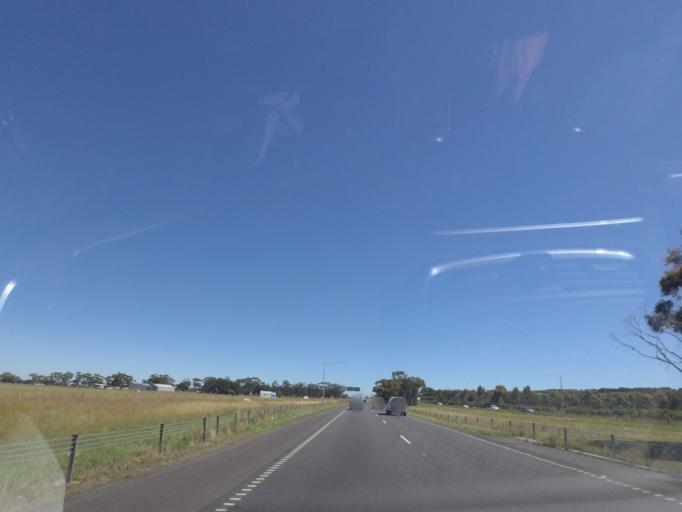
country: AU
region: Victoria
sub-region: Hume
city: Craigieburn
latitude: -37.5592
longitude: 144.9429
